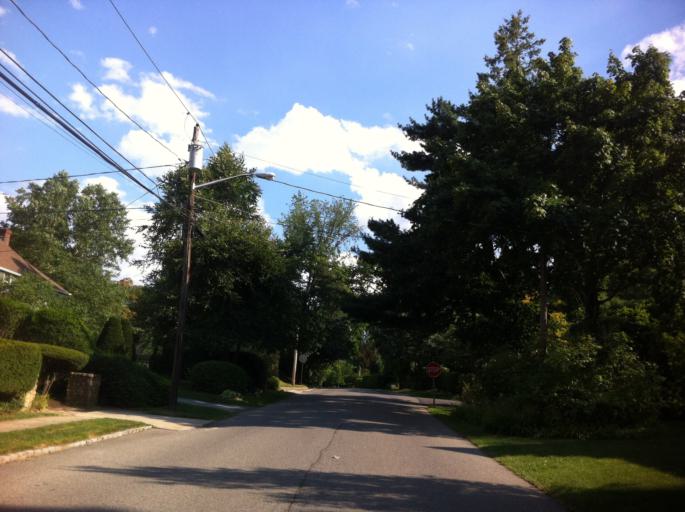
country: US
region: New York
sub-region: Nassau County
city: Sea Cliff
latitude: 40.8439
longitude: -73.6458
